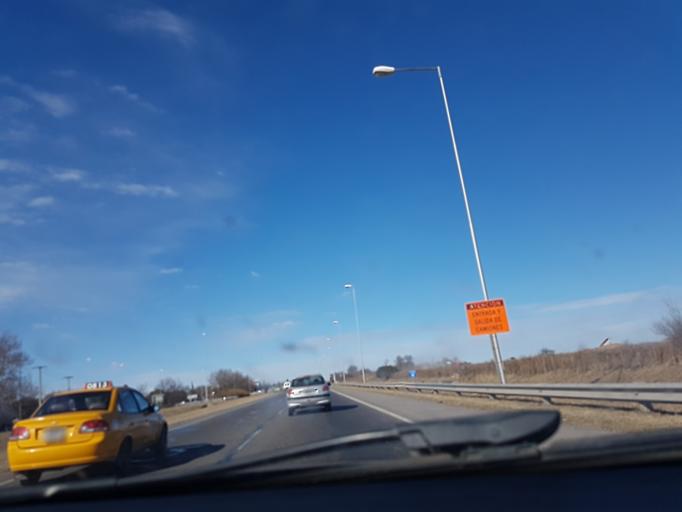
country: AR
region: Cordoba
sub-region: Departamento de Capital
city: Cordoba
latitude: -31.4078
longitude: -64.2697
